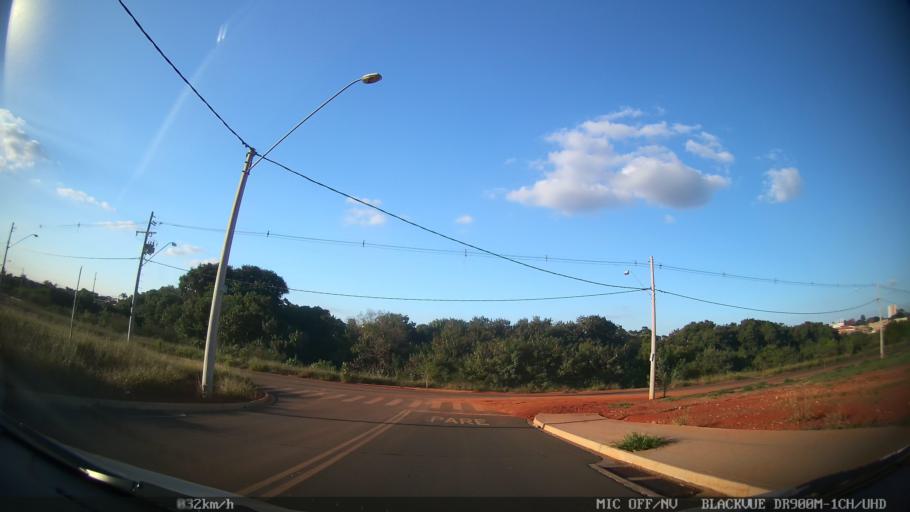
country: BR
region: Sao Paulo
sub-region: Santa Barbara D'Oeste
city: Santa Barbara d'Oeste
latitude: -22.7438
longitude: -47.3875
